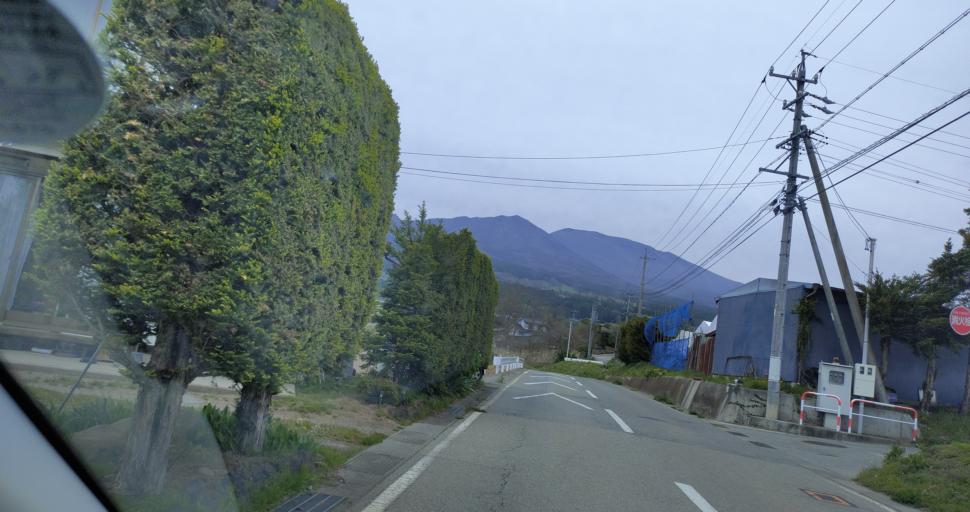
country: JP
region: Nagano
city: Komoro
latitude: 36.3314
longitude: 138.4893
